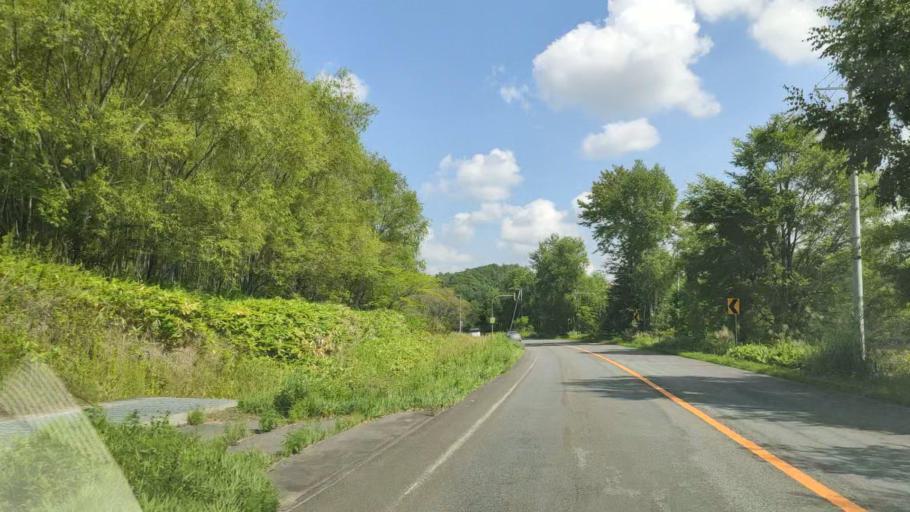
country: JP
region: Hokkaido
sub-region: Asahikawa-shi
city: Asahikawa
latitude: 43.5729
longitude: 142.4386
